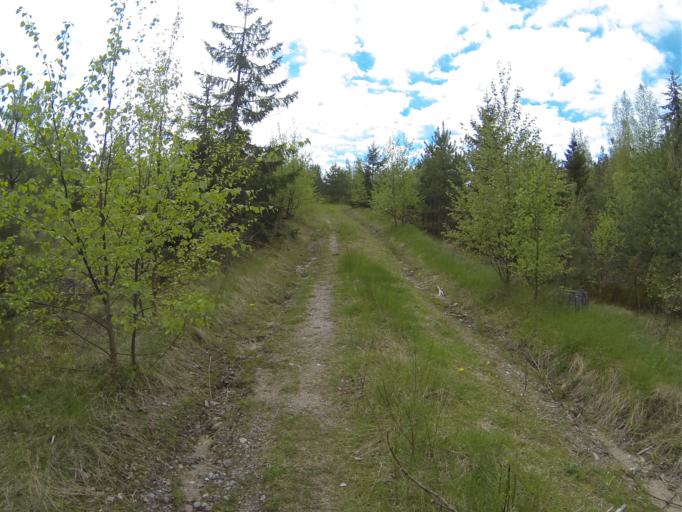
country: FI
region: Varsinais-Suomi
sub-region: Salo
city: Halikko
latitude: 60.3270
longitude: 23.0659
